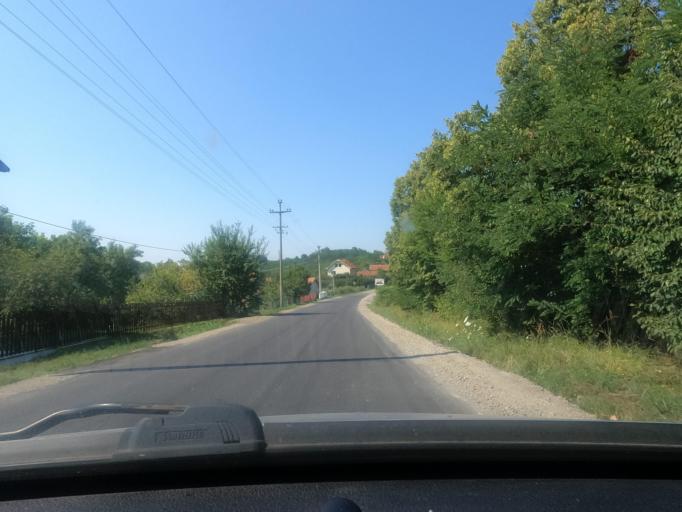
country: RS
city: Kozjak
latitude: 44.5700
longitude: 19.2864
